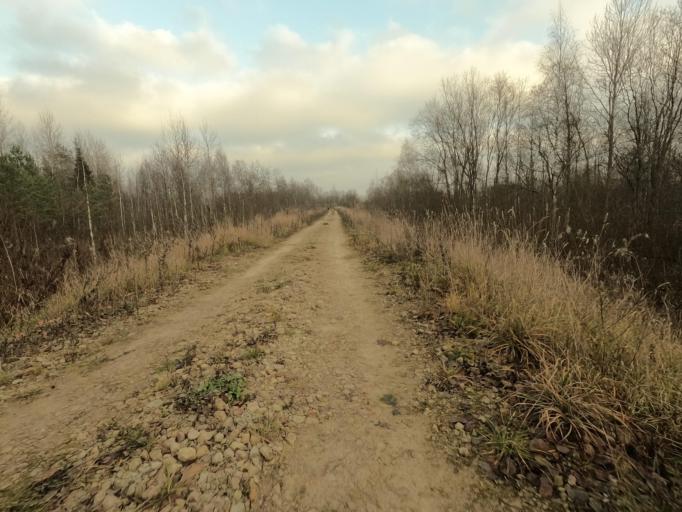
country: RU
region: Leningrad
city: Mga
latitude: 59.7531
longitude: 31.0735
